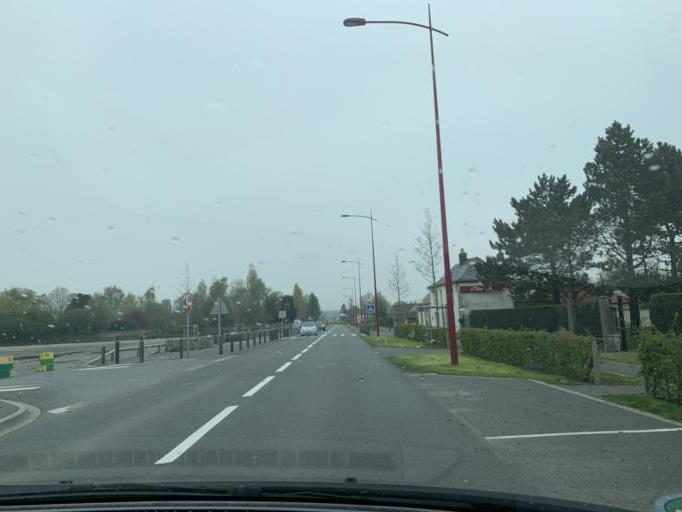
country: FR
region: Picardie
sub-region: Departement de la Somme
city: Nouvion
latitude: 50.1717
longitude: 1.8105
